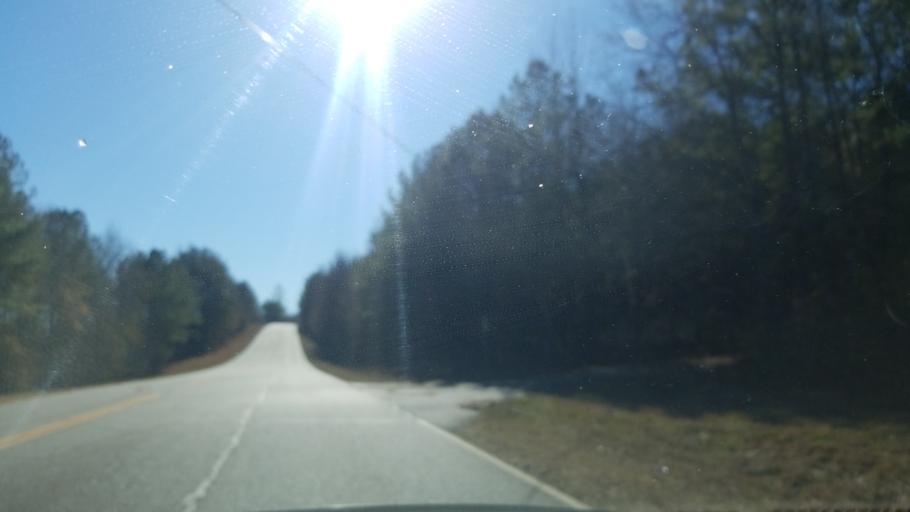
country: US
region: Georgia
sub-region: Talbot County
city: Sardis
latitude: 32.8154
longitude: -84.6470
